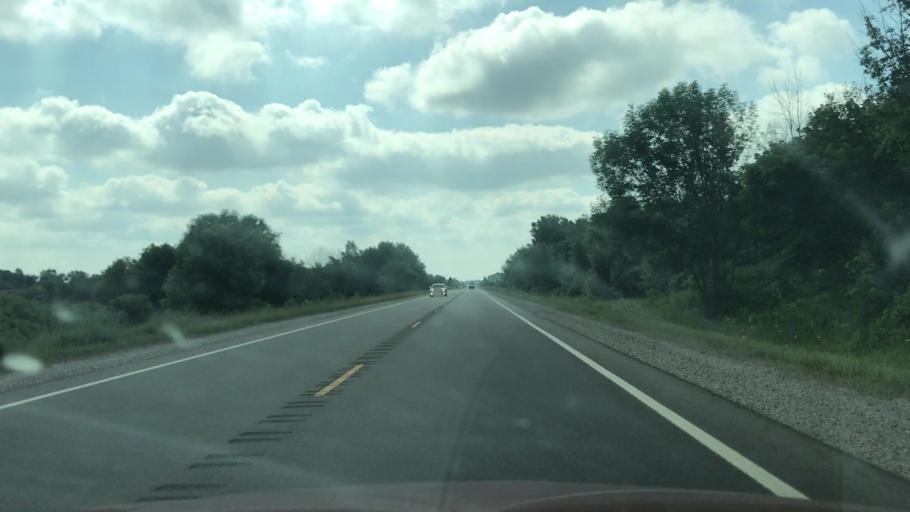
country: US
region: Michigan
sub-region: Kent County
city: Kent City
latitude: 43.2159
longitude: -85.7587
